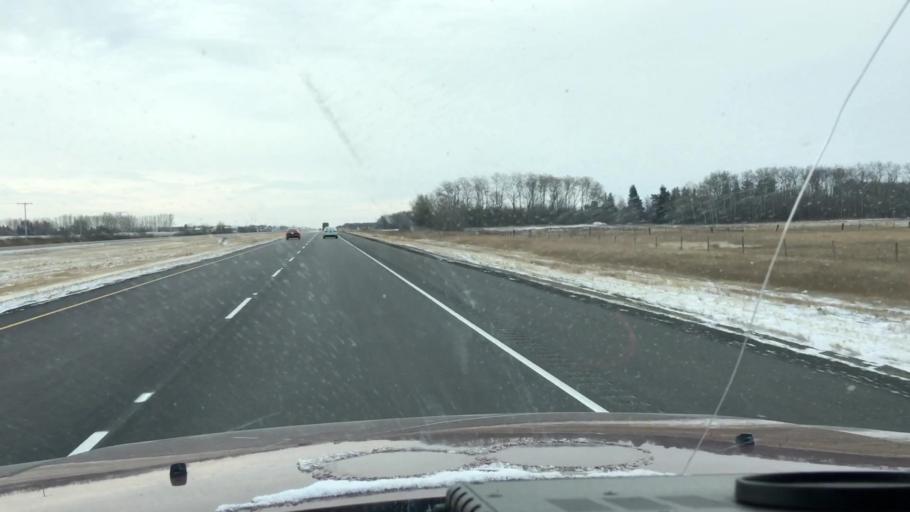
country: CA
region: Saskatchewan
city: Saskatoon
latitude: 51.9775
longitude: -106.5576
